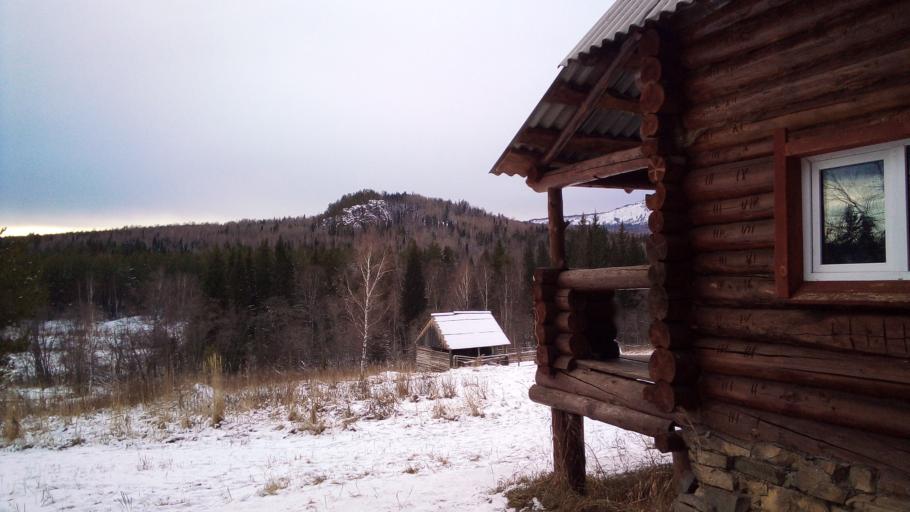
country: RU
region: Chelyabinsk
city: Satka
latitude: 54.8164
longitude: 59.0031
